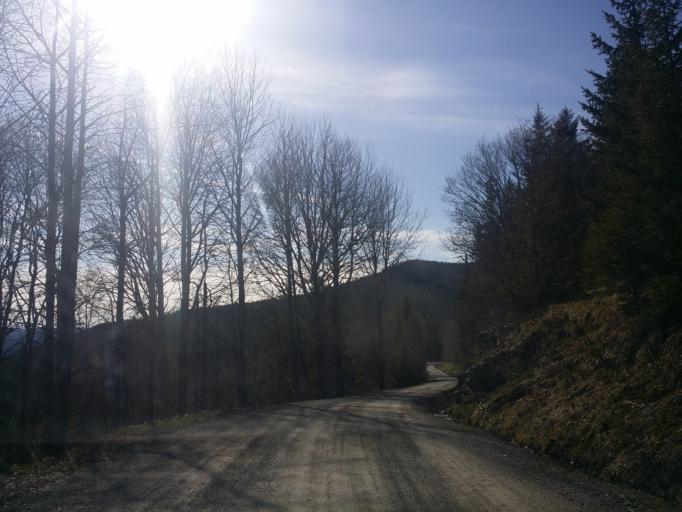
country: NO
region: Telemark
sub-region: Seljord
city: Seljord
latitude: 59.6203
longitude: 8.6917
